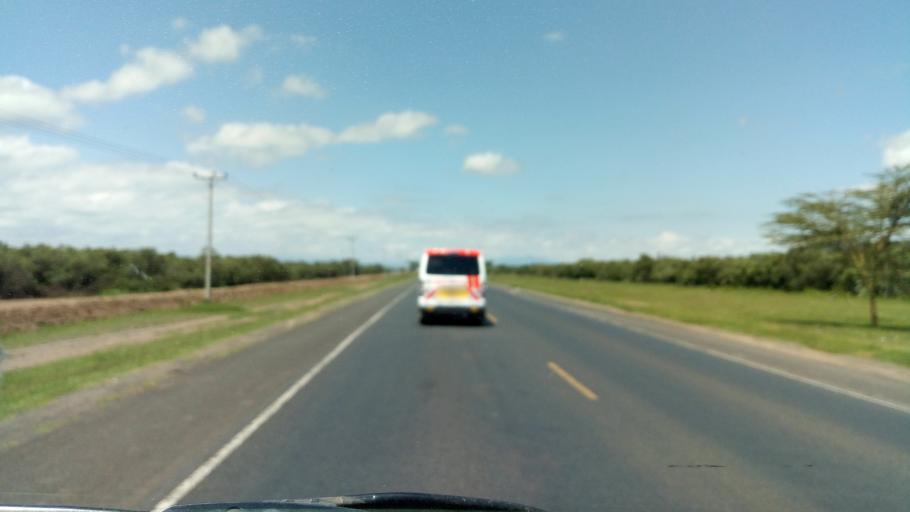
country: KE
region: Nakuru
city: Naivasha
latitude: -0.5555
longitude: 36.3502
